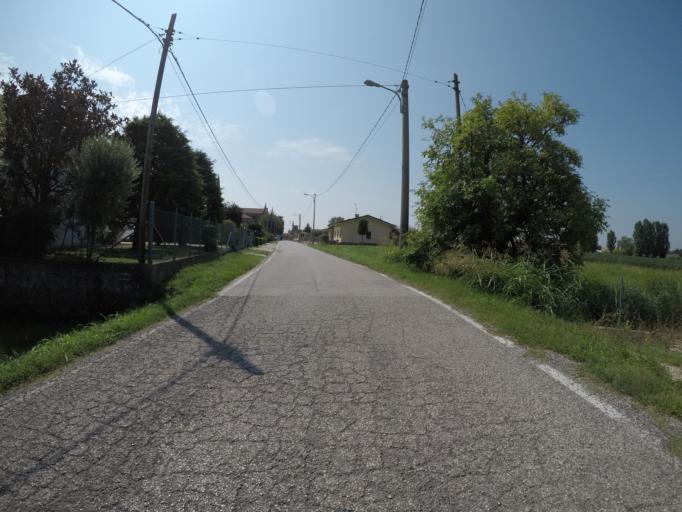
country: IT
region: Veneto
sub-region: Provincia di Rovigo
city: Lendinara
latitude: 45.1035
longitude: 11.5914
